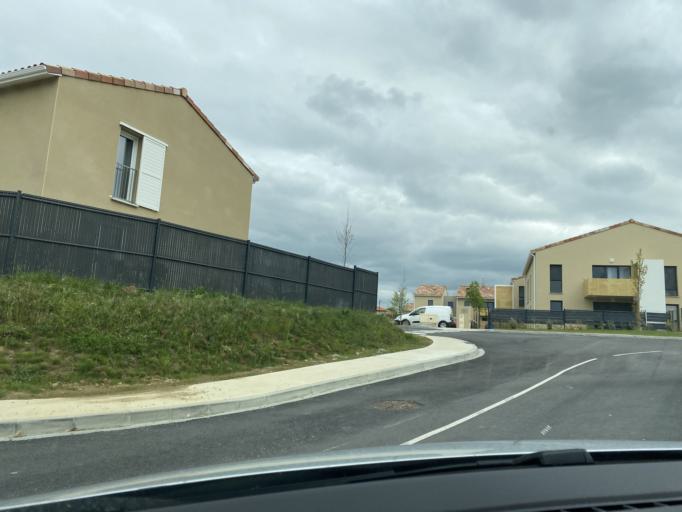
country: FR
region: Midi-Pyrenees
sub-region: Departement de la Haute-Garonne
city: Ayguesvives
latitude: 43.4291
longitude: 1.5936
